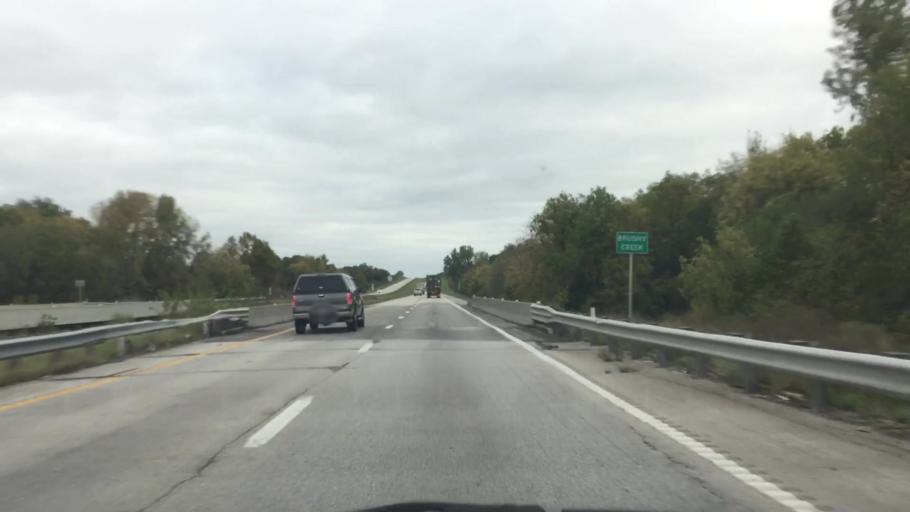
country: US
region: Missouri
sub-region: Clinton County
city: Cameron
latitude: 39.6801
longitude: -94.2325
